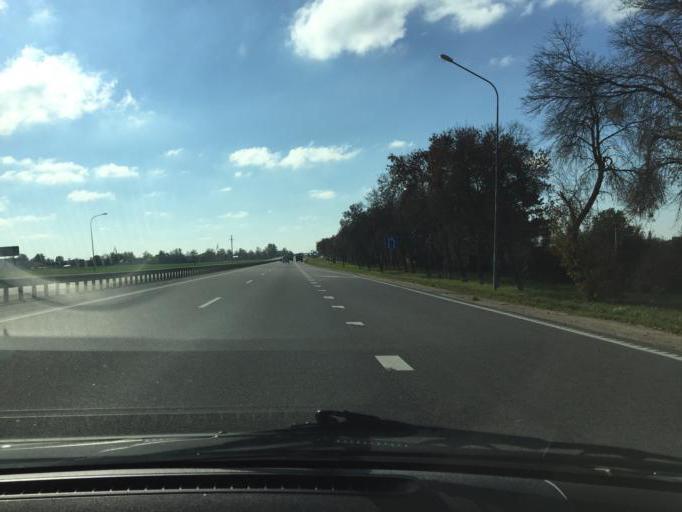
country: BY
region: Minsk
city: Slutsk
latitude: 53.0804
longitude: 27.5651
